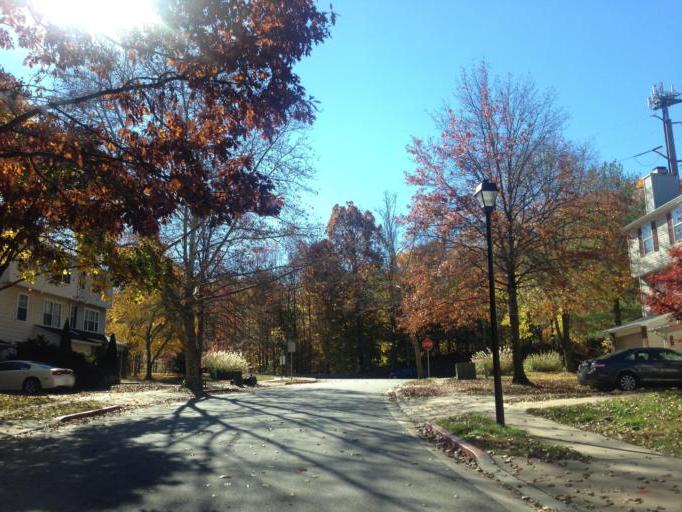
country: US
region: Maryland
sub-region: Howard County
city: Riverside
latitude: 39.2076
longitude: -76.8721
